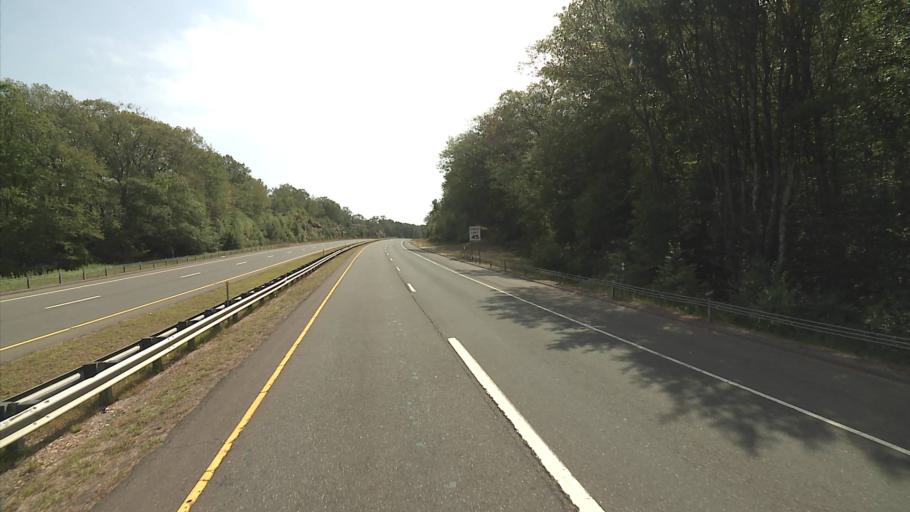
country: US
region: Connecticut
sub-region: New London County
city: Niantic
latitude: 41.3235
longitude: -72.2483
